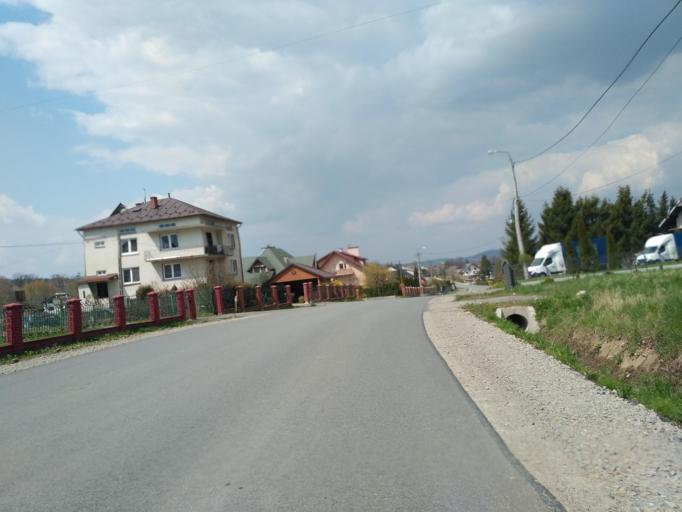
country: PL
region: Subcarpathian Voivodeship
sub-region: Powiat sanocki
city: Strachocina
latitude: 49.5796
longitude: 22.1216
